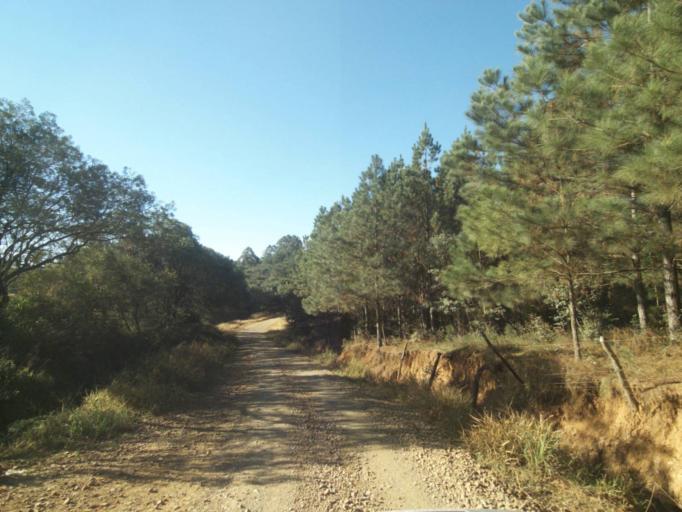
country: BR
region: Parana
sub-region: Tibagi
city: Tibagi
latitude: -24.5474
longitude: -50.5121
